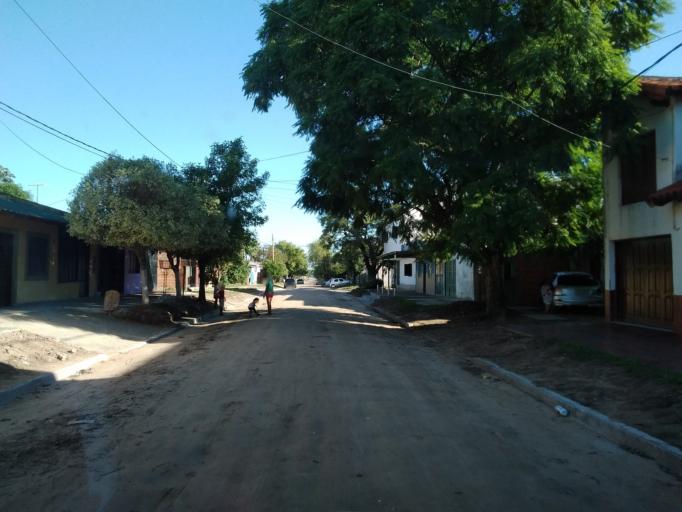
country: AR
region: Corrientes
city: Corrientes
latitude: -27.5034
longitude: -58.7824
